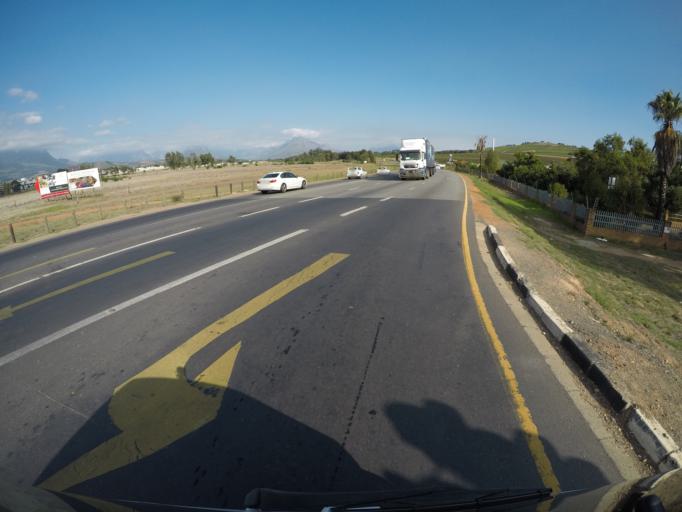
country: ZA
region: Western Cape
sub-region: Cape Winelands District Municipality
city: Stellenbosch
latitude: -33.8751
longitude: 18.8139
